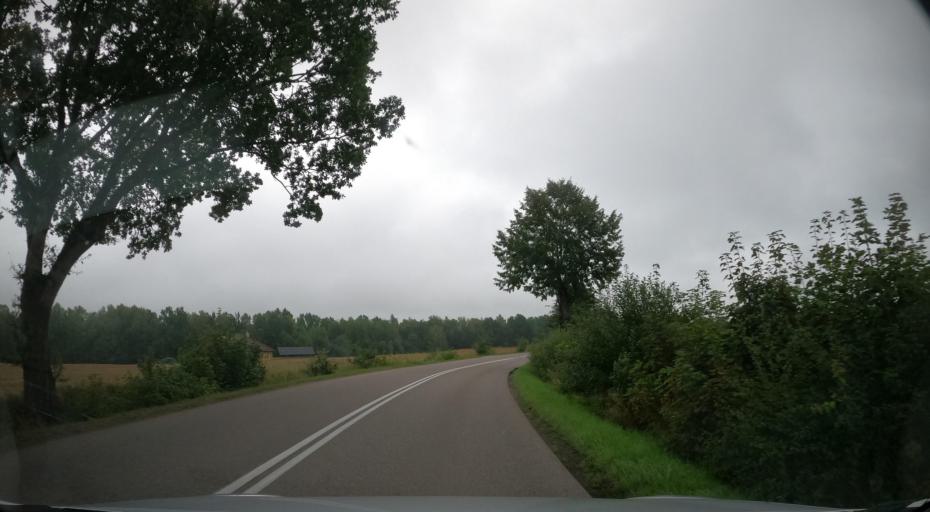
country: PL
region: Pomeranian Voivodeship
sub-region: Powiat wejherowski
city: Linia
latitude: 54.4604
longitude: 18.0427
